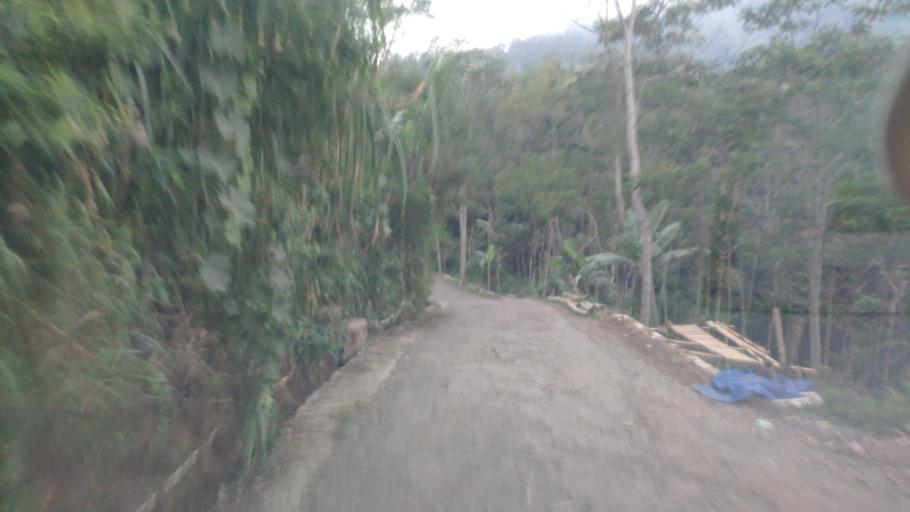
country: ID
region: Central Java
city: Wonosobo
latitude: -7.2793
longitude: 109.7296
